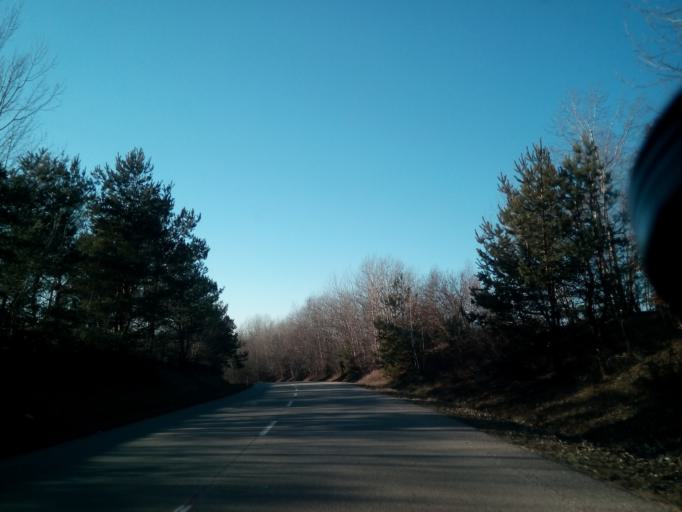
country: SK
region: Kosicky
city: Moldava nad Bodvou
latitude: 48.6913
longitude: 21.0532
